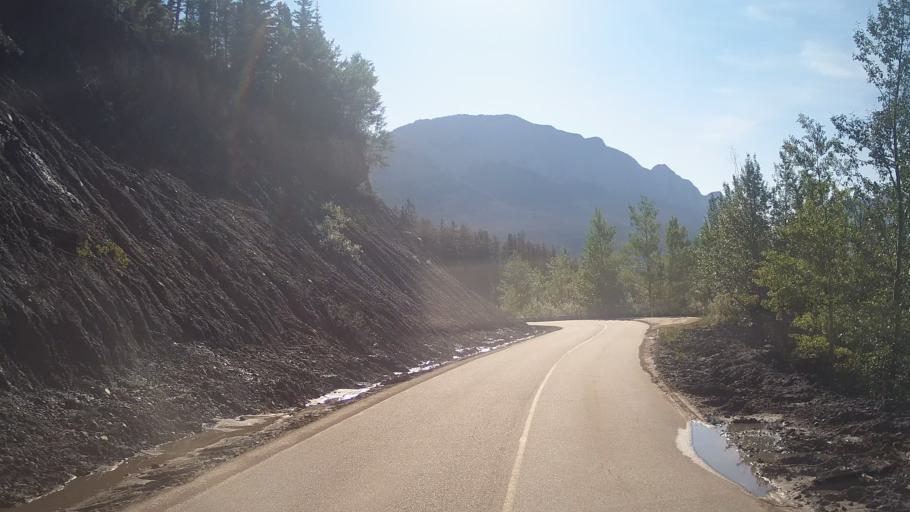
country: CA
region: Alberta
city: Hinton
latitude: 53.1778
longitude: -117.8474
